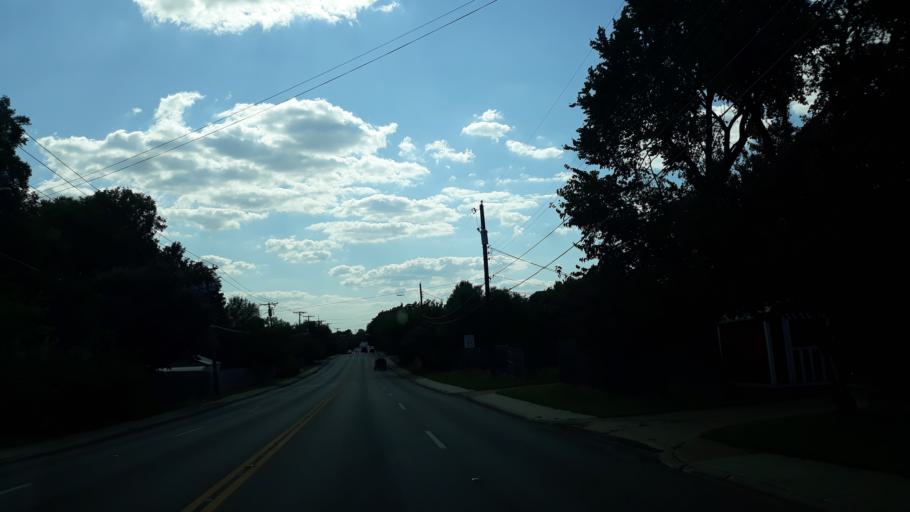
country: US
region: Texas
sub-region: Dallas County
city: Irving
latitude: 32.8509
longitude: -96.9848
